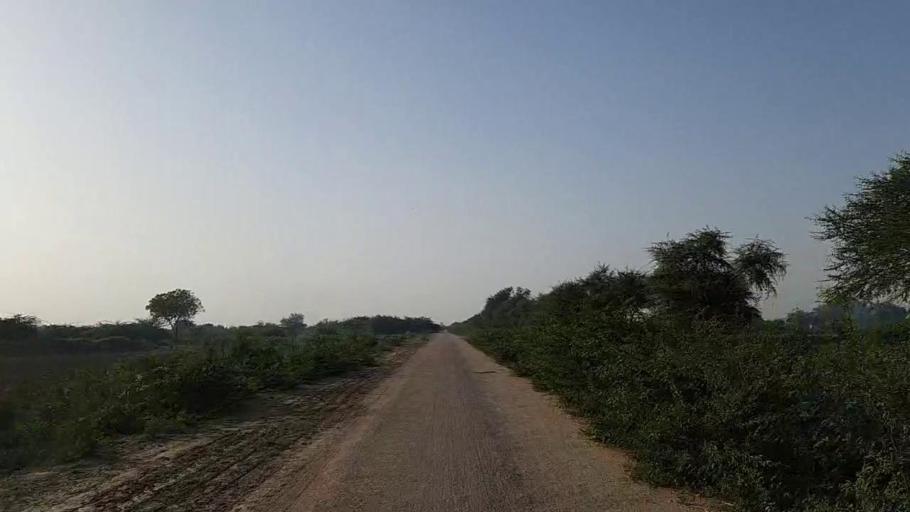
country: PK
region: Sindh
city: Jati
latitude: 24.3354
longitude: 68.1539
